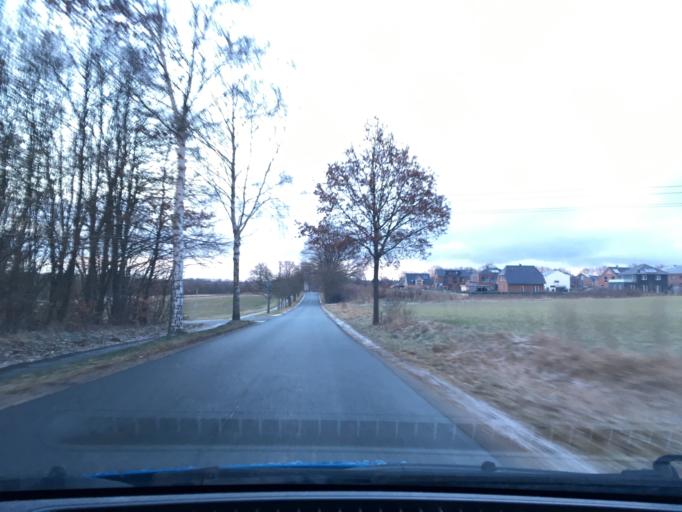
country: DE
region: Lower Saxony
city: Reppenstedt
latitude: 53.2238
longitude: 10.3670
